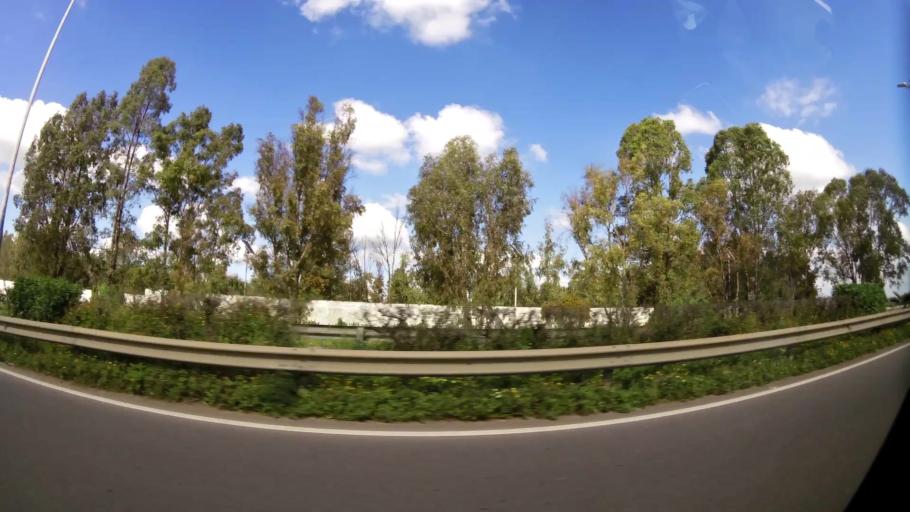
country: MA
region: Chaouia-Ouardigha
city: Nouaseur
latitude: 33.4029
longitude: -7.6229
